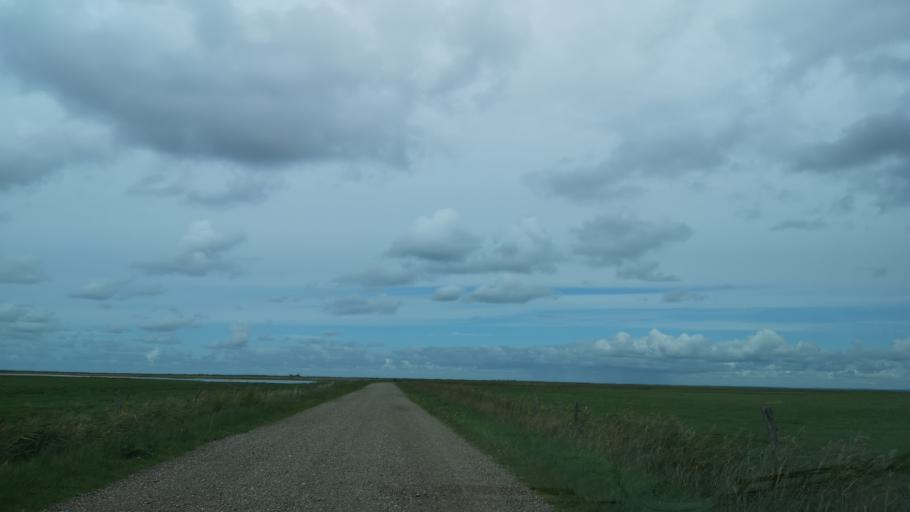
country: DK
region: Central Jutland
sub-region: Ringkobing-Skjern Kommune
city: Hvide Sande
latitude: 55.8653
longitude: 8.2204
